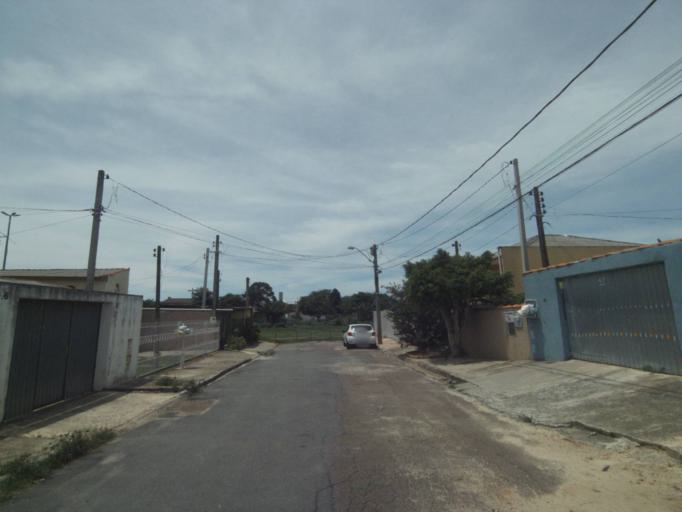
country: BR
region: Parana
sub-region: Curitiba
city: Curitiba
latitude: -25.5037
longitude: -49.3369
